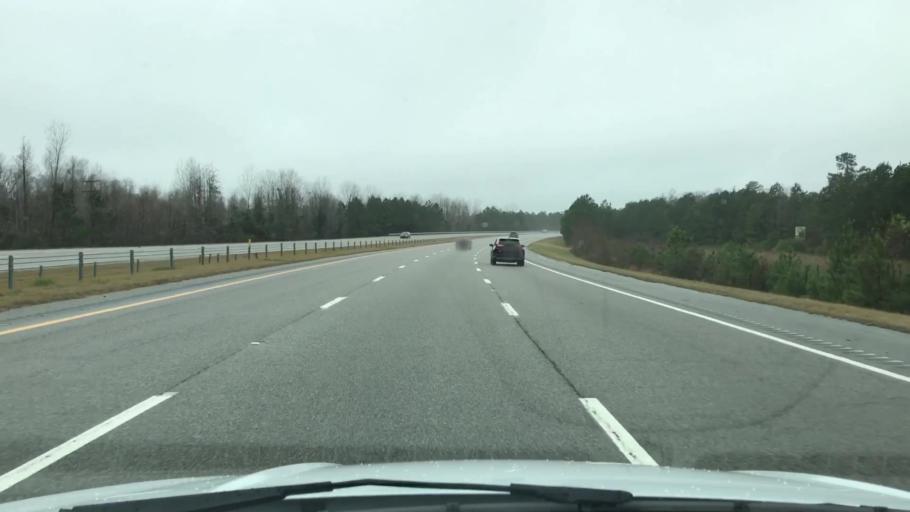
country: US
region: South Carolina
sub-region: Horry County
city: Myrtle Beach
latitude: 33.7491
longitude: -78.8786
